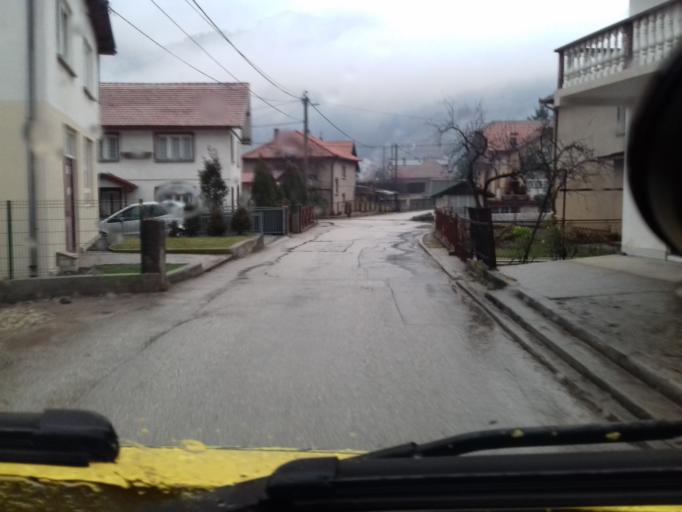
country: BA
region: Federation of Bosnia and Herzegovina
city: Zeljezno Polje
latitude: 44.3317
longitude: 17.9117
